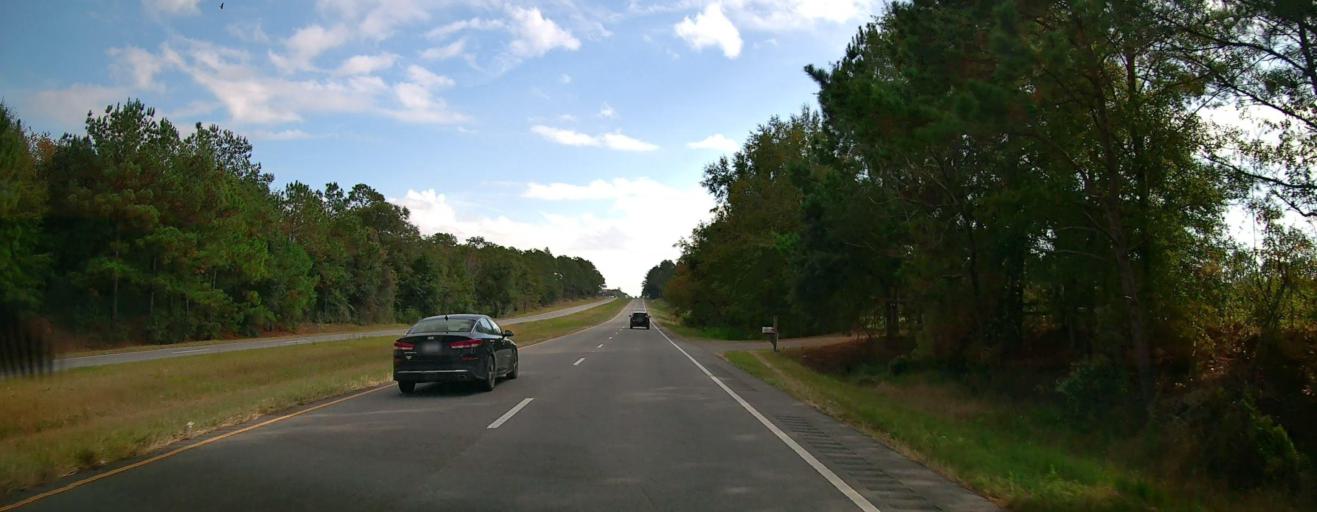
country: US
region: Georgia
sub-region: Thomas County
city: Meigs
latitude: 30.9845
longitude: -84.0407
